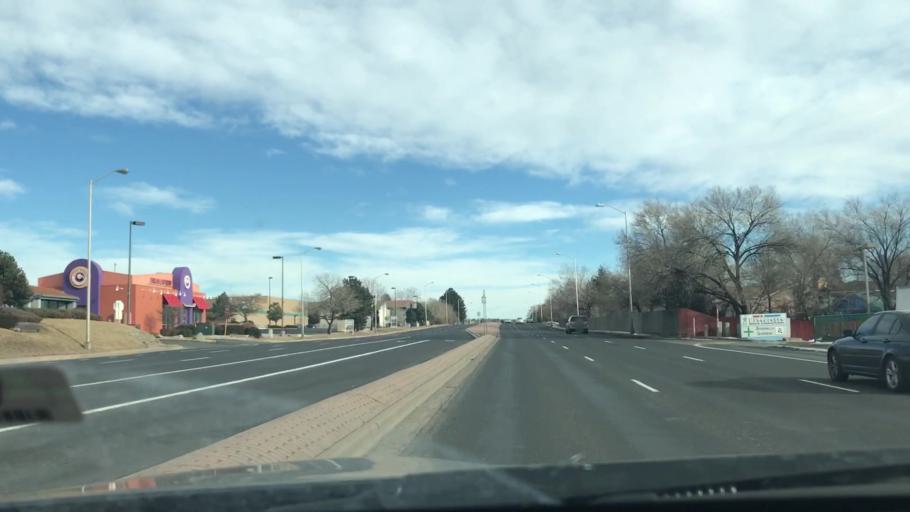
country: US
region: Colorado
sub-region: El Paso County
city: Colorado Springs
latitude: 38.9042
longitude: -104.7748
